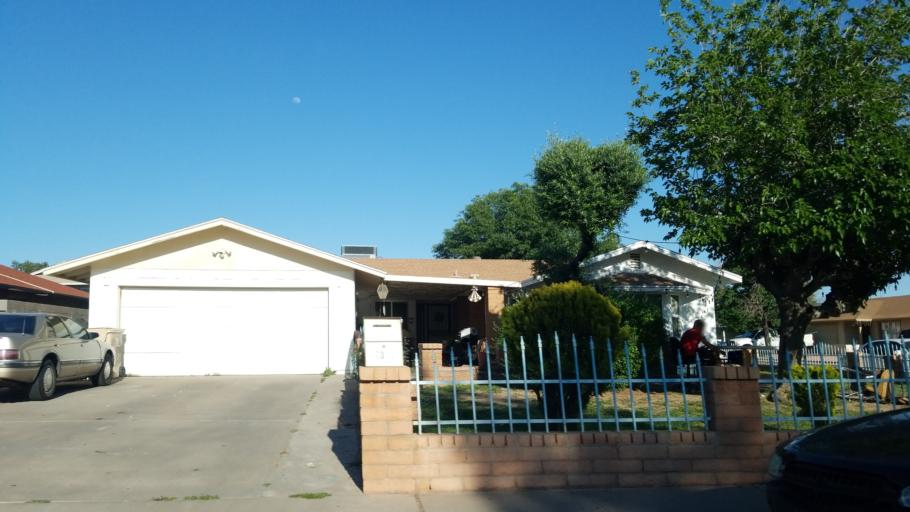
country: US
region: Arizona
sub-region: Maricopa County
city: Glendale
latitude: 33.5226
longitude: -112.1601
